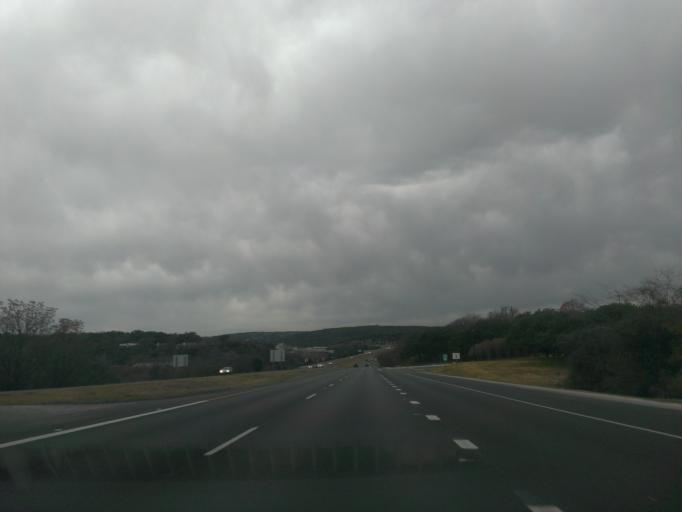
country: US
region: Texas
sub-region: Williamson County
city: Jollyville
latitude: 30.3887
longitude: -97.7498
